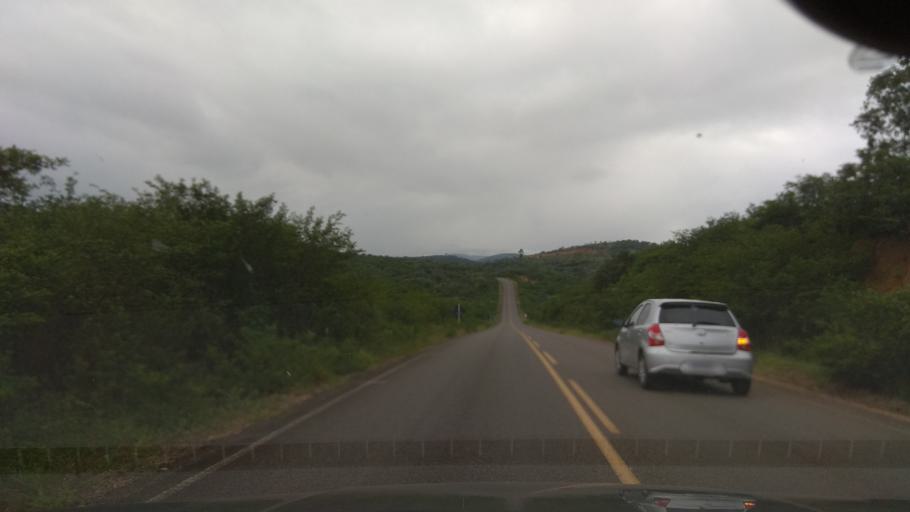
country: BR
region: Bahia
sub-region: Santa Ines
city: Santa Ines
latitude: -13.2720
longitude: -39.8046
